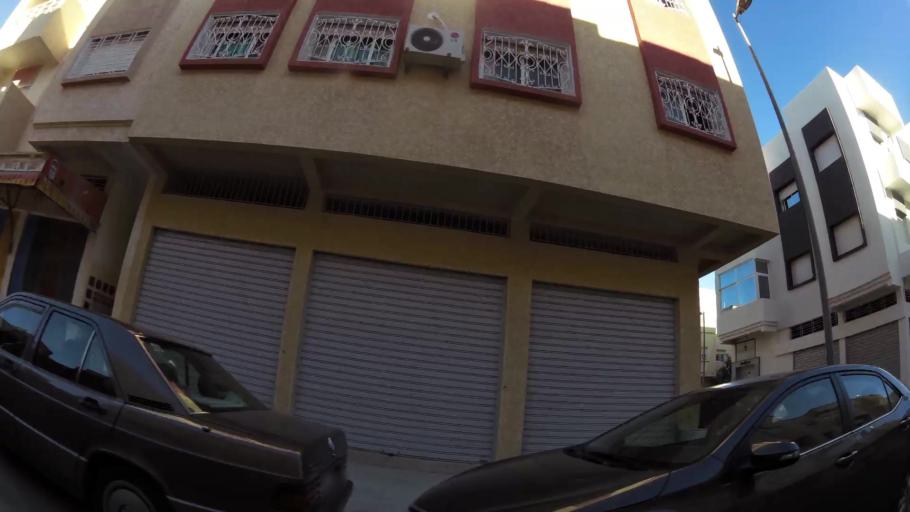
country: MA
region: Fes-Boulemane
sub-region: Fes
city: Fes
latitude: 34.0070
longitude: -5.0143
